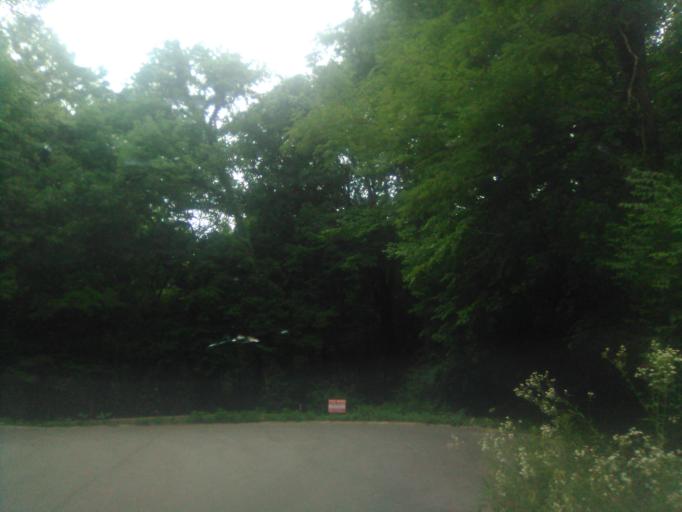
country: US
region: Tennessee
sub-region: Davidson County
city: Forest Hills
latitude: 36.0679
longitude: -86.8653
